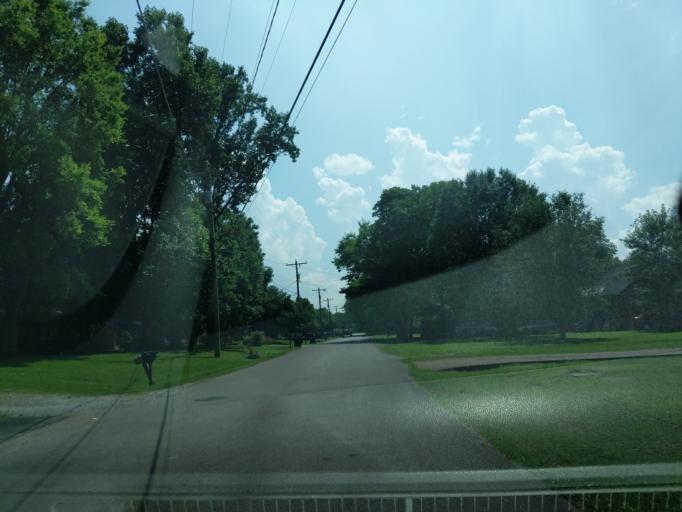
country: US
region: Tennessee
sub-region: Davidson County
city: Lakewood
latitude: 36.2811
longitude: -86.6746
